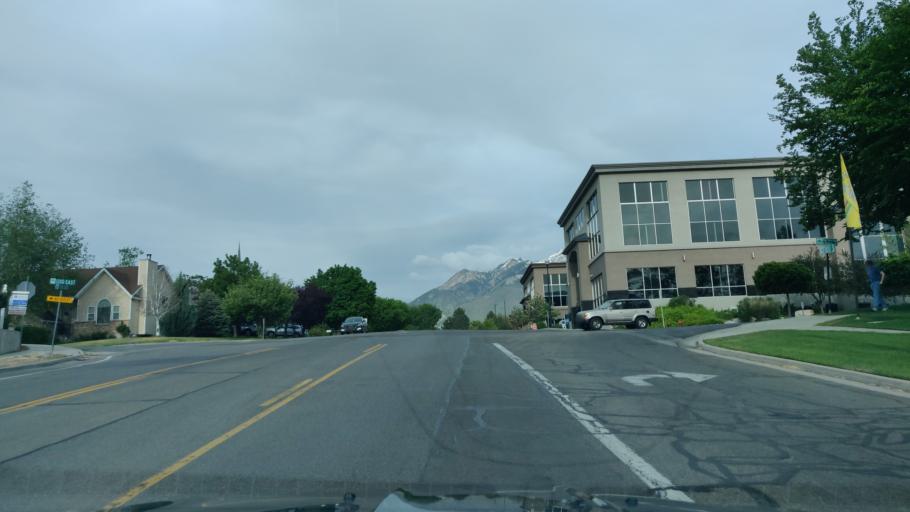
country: US
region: Utah
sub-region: Salt Lake County
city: Little Cottonwood Creek Valley
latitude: 40.6096
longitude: -111.8579
